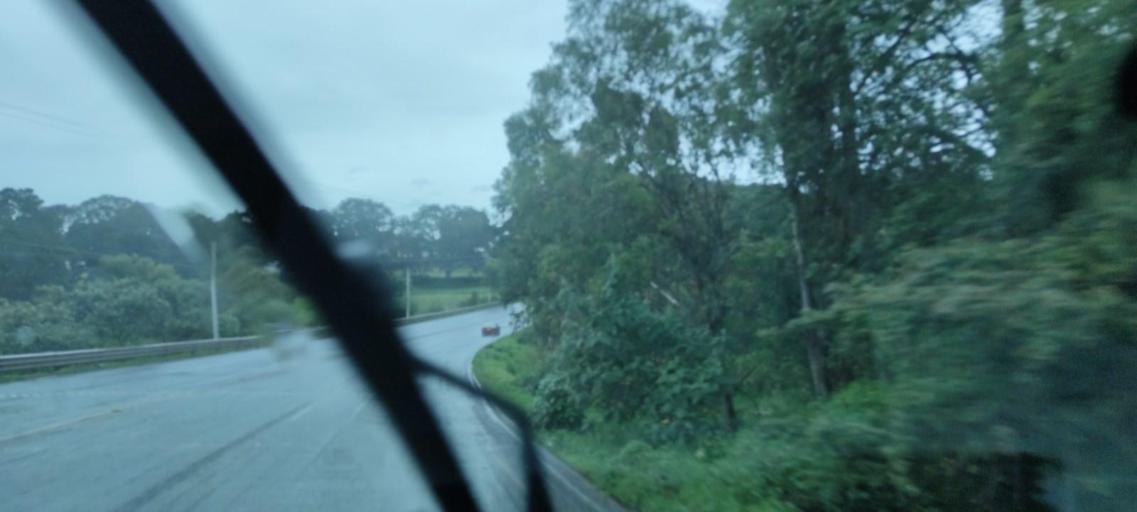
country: MX
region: Mexico
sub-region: Jilotepec
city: Doxhicho
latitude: 19.9372
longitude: -99.5664
